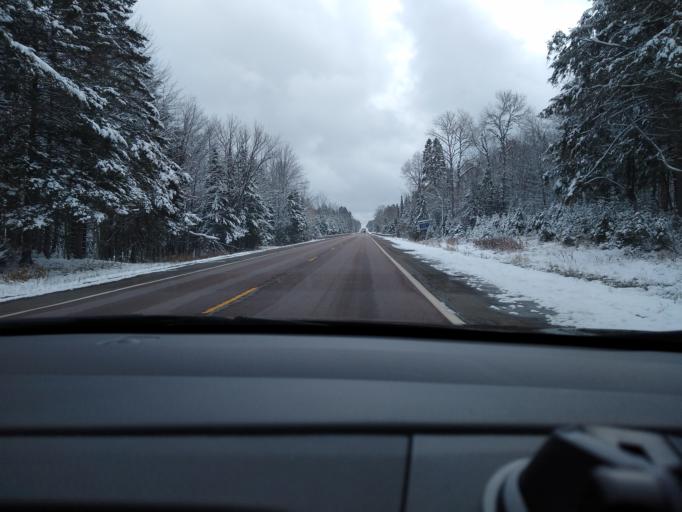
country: US
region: Wisconsin
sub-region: Vilas County
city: Eagle River
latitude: 46.2130
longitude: -89.0398
